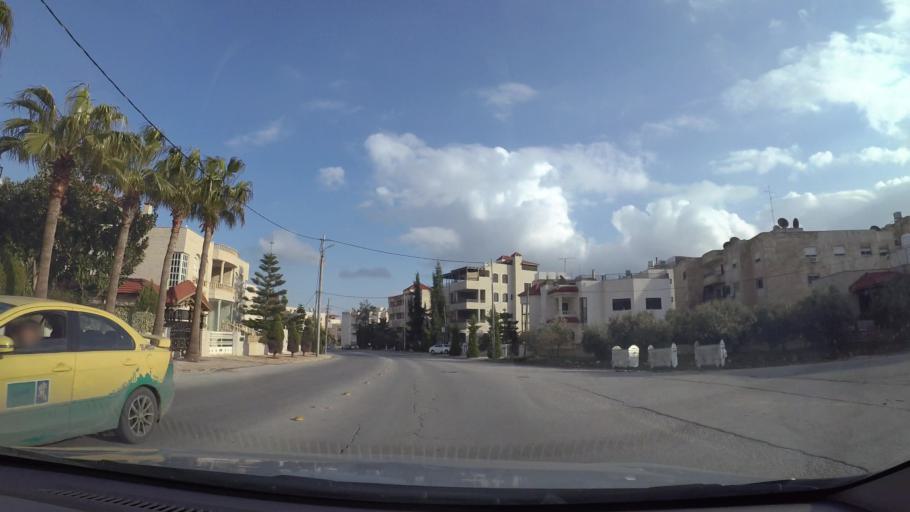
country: JO
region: Amman
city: Wadi as Sir
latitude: 31.9818
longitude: 35.8513
